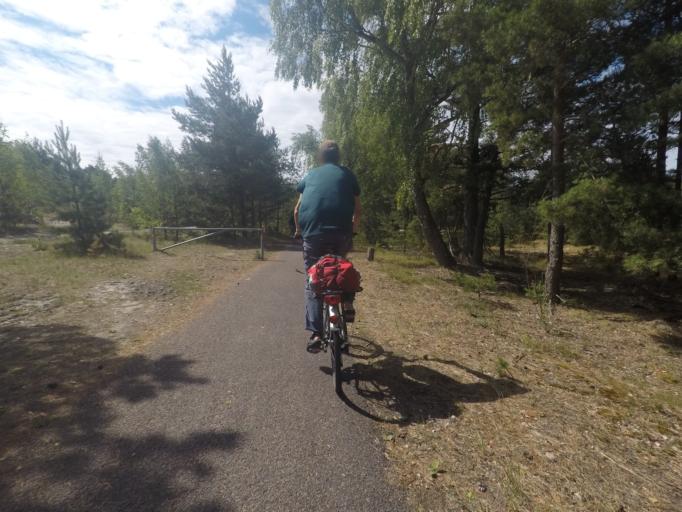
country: LT
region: Klaipedos apskritis
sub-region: Klaipeda
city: Klaipeda
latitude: 55.5686
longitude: 21.1126
